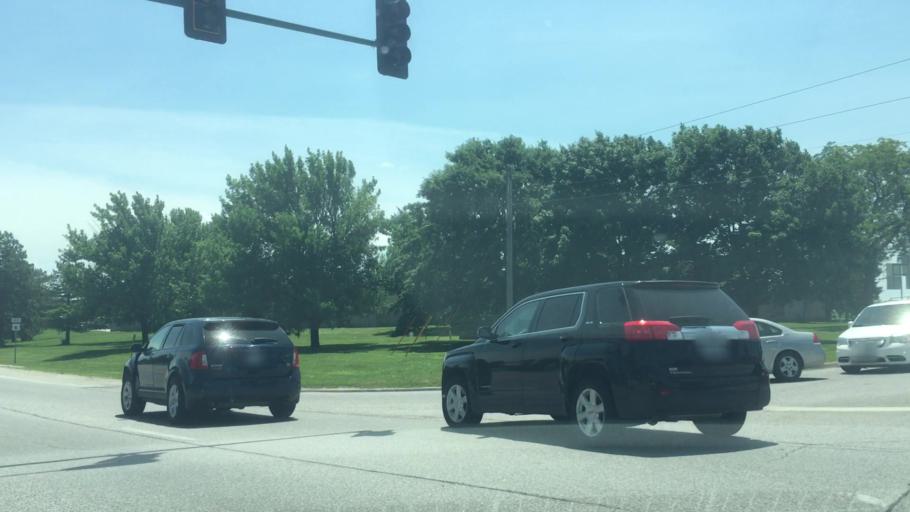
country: US
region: Iowa
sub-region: Johnson County
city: Iowa City
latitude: 41.6475
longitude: -91.5400
